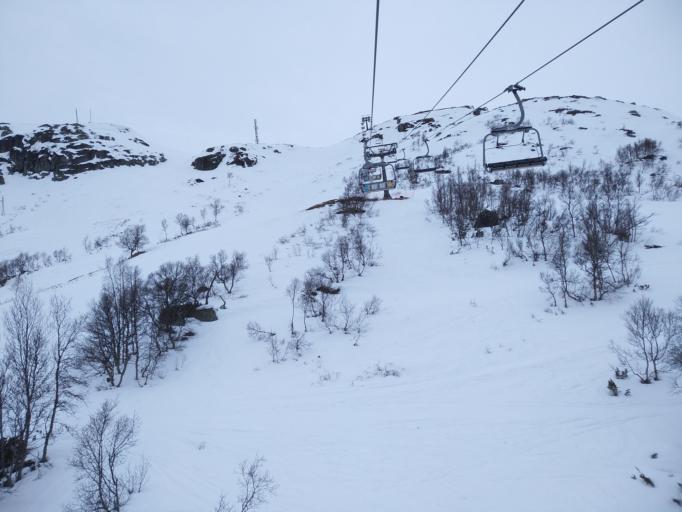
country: NO
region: Aust-Agder
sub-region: Bykle
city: Hovden
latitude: 59.5760
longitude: 7.3381
